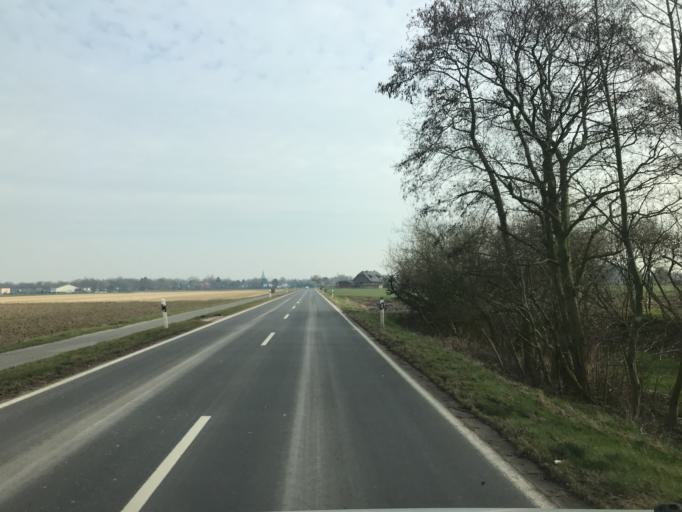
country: DE
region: North Rhine-Westphalia
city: Kempen
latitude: 51.3651
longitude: 6.3951
